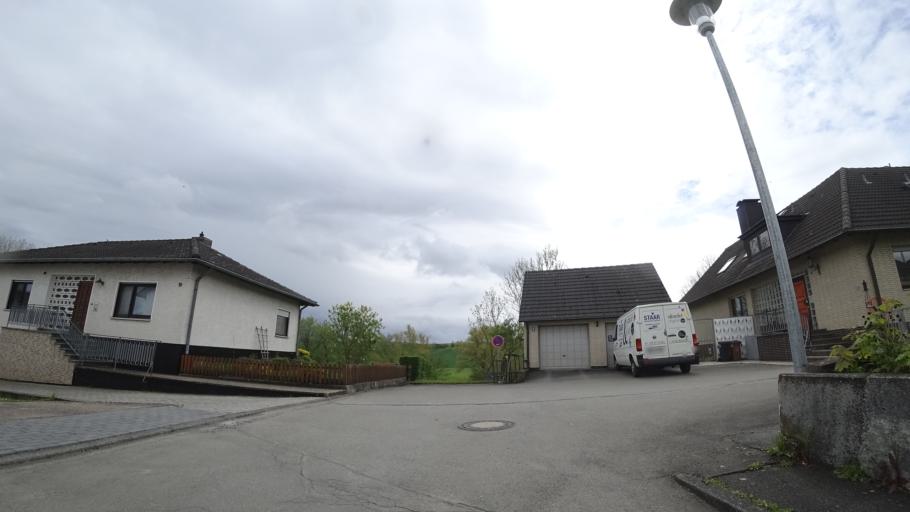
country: DE
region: Hesse
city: Liebenau
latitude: 51.4569
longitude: 9.3128
